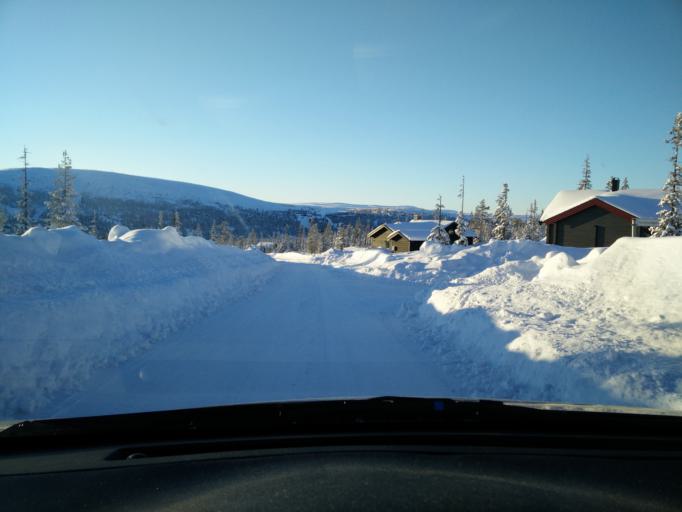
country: SE
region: Jaemtland
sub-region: Bergs Kommun
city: Hoverberg
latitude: 62.4960
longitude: 14.1304
